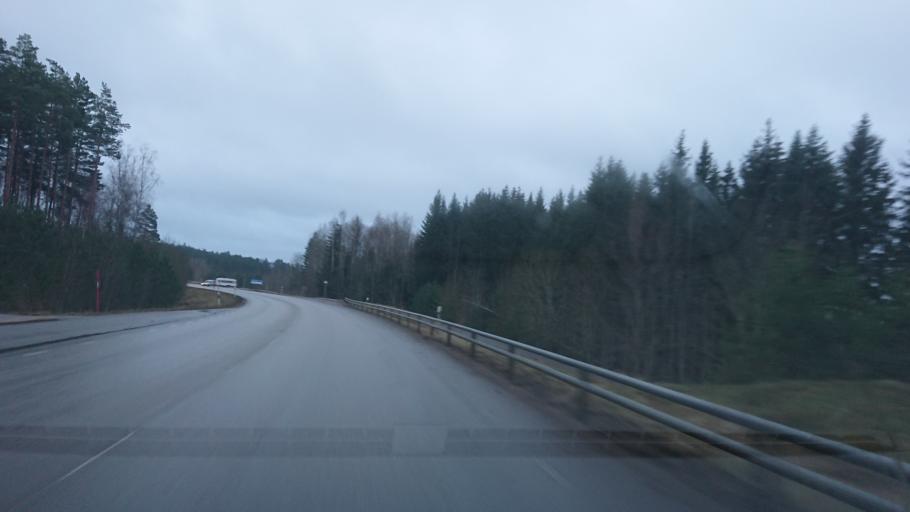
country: SE
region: Uppsala
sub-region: Osthammars Kommun
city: Bjorklinge
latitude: 60.0120
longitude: 17.5884
